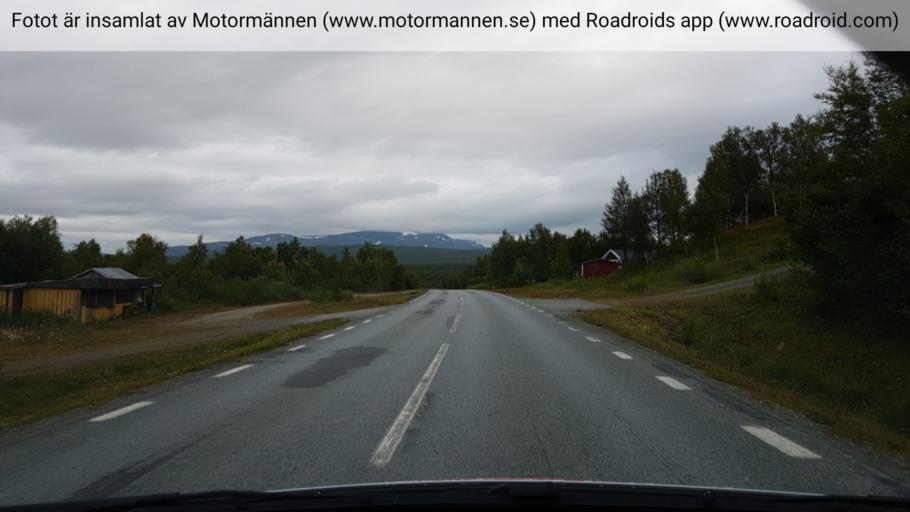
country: NO
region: Nordland
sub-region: Rana
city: Mo i Rana
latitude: 66.0027
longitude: 15.0913
